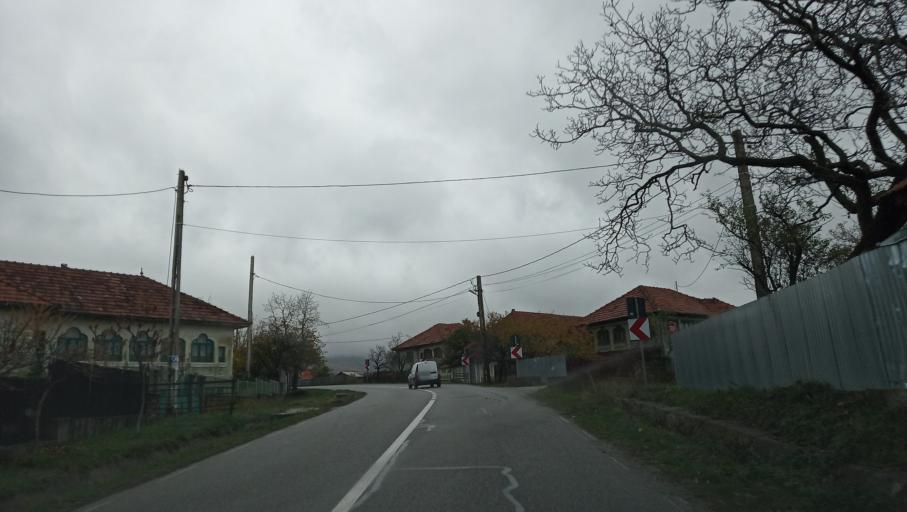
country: RO
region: Gorj
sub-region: Comuna Crasna
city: Crasna
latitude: 45.1674
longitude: 23.4830
